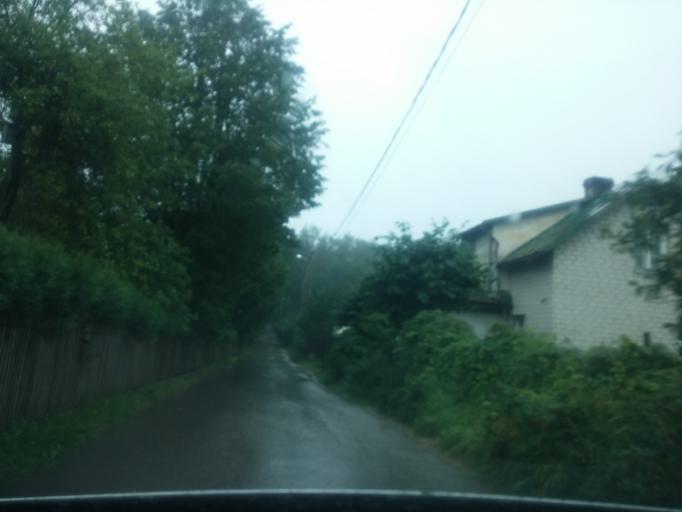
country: LV
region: Ikskile
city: Ikskile
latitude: 56.8410
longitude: 24.4946
